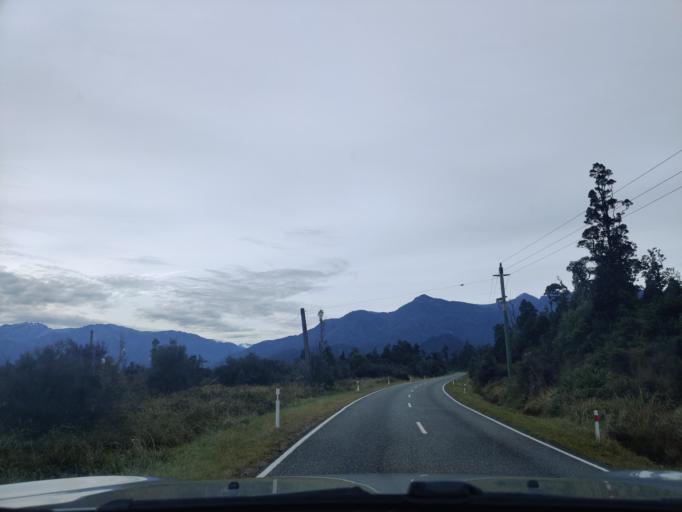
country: NZ
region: West Coast
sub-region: Westland District
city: Hokitika
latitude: -43.2576
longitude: 170.2803
